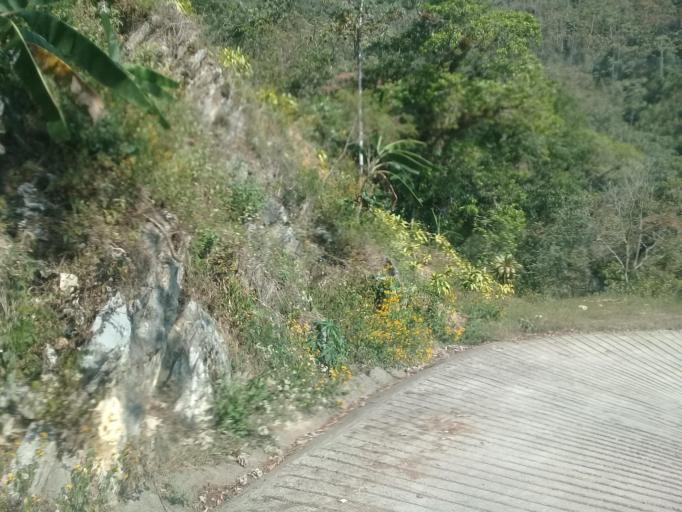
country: MX
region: Veracruz
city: Rafael Delgado
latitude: 18.7833
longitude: -97.0256
